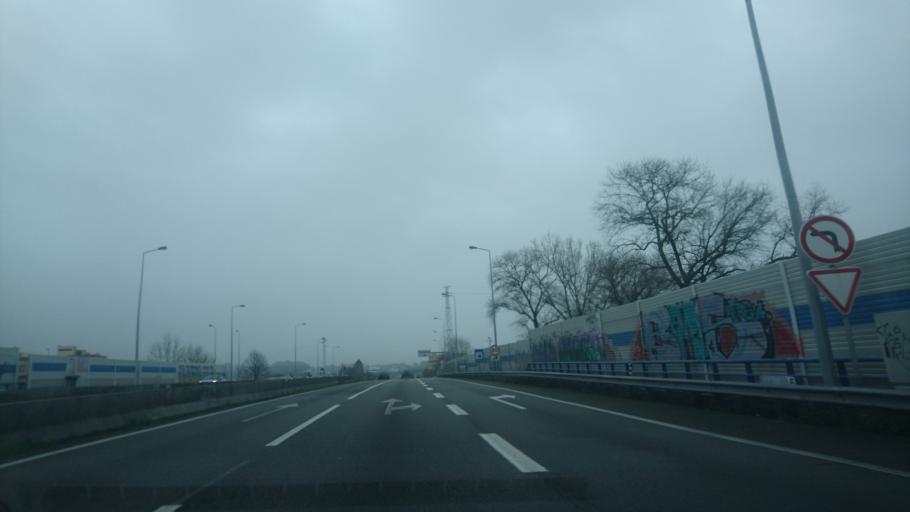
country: PT
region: Porto
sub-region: Vila Nova de Gaia
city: Vilar do Paraiso
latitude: 41.0985
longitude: -8.6271
